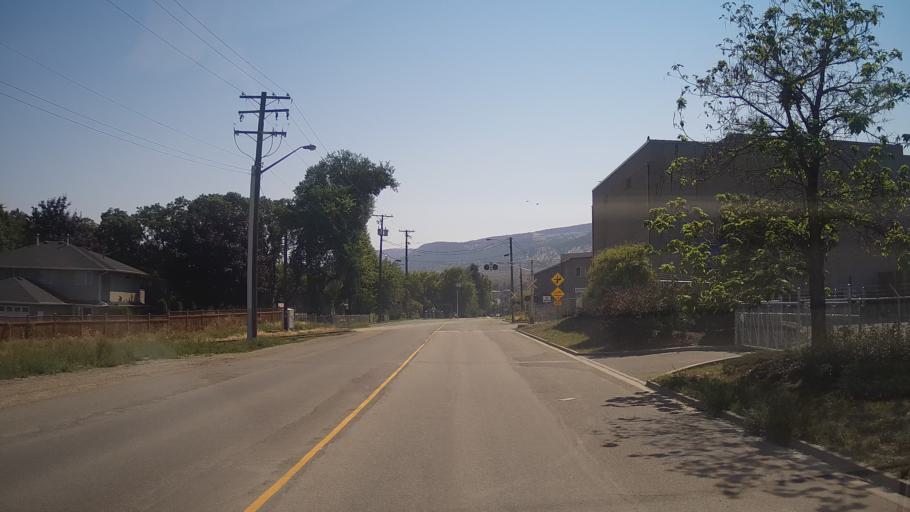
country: CA
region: British Columbia
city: Kamloops
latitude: 50.6776
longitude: -120.3221
